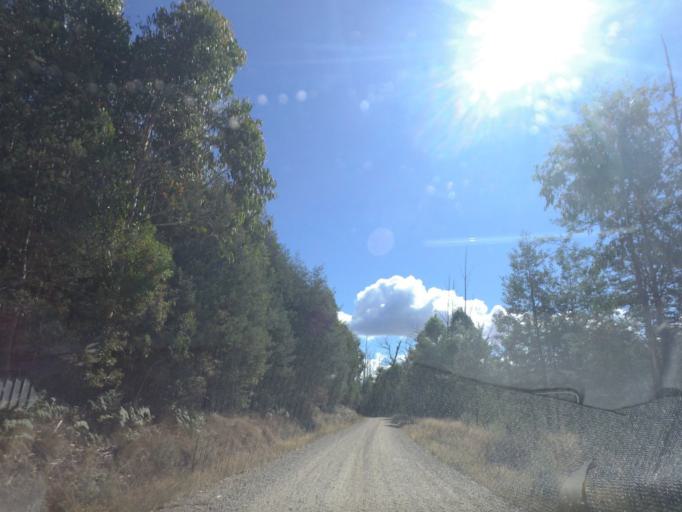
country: AU
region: Victoria
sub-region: Murrindindi
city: Alexandra
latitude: -37.4108
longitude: 145.8048
